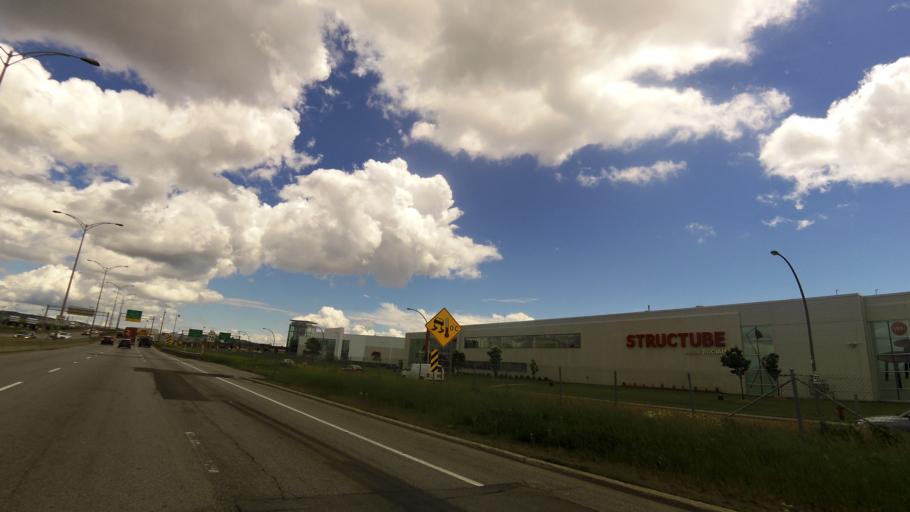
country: CA
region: Quebec
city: Saint-Laurent
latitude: 45.4947
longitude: -73.6833
